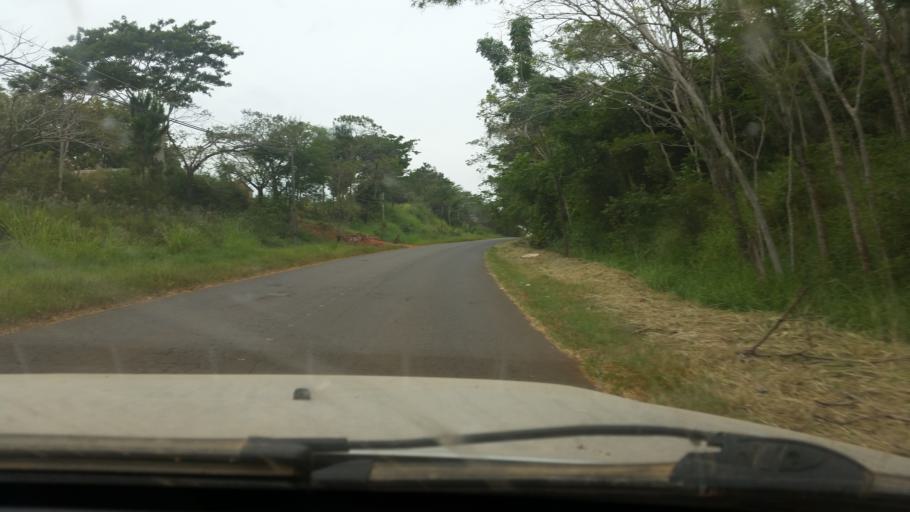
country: PY
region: Guaira
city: Independencia
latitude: -25.7020
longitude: -56.1966
